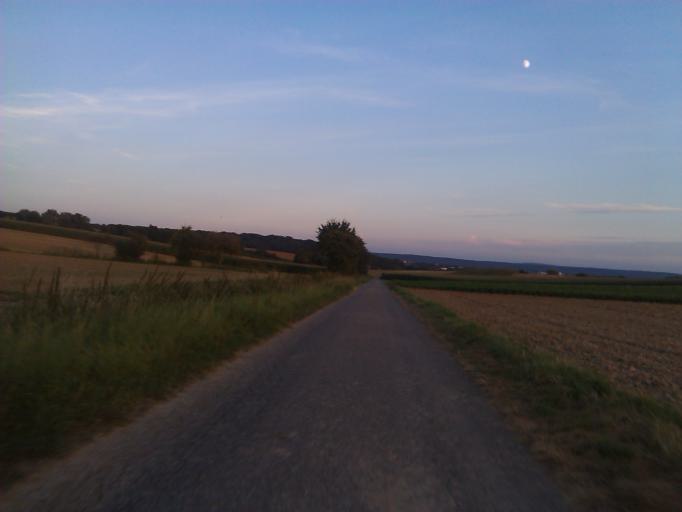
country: DE
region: Baden-Wuerttemberg
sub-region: Regierungsbezirk Stuttgart
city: Ittlingen
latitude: 49.1883
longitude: 8.8733
